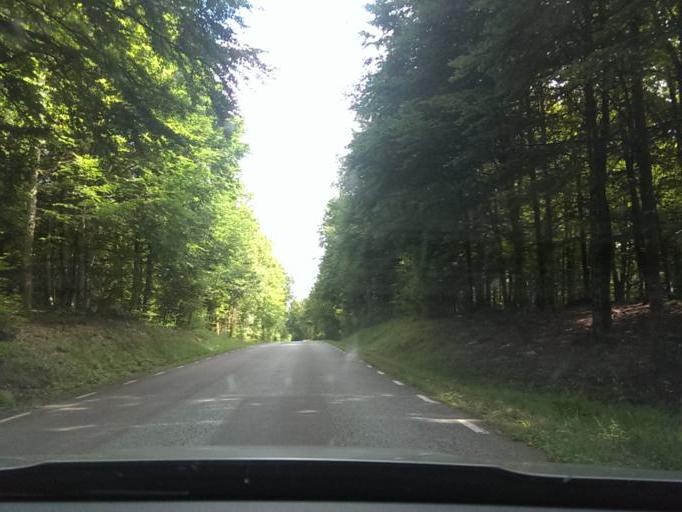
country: SE
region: Joenkoeping
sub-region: Varnamo Kommun
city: Forsheda
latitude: 57.0460
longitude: 13.8900
